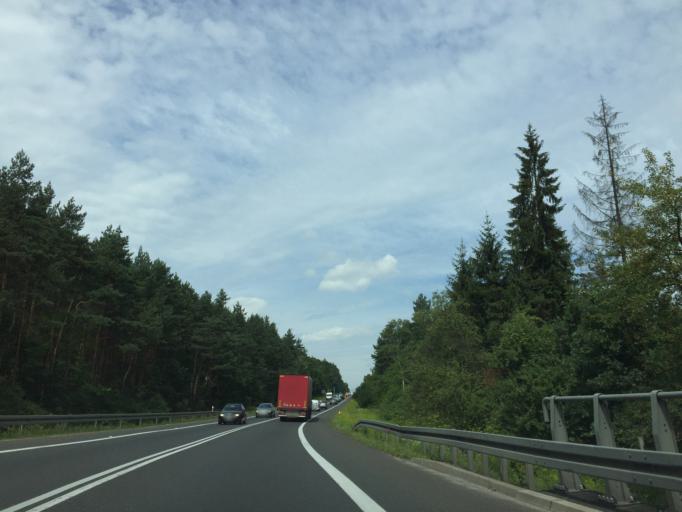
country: PL
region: Lesser Poland Voivodeship
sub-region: Powiat olkuski
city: Osiek
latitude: 50.2602
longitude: 19.6270
